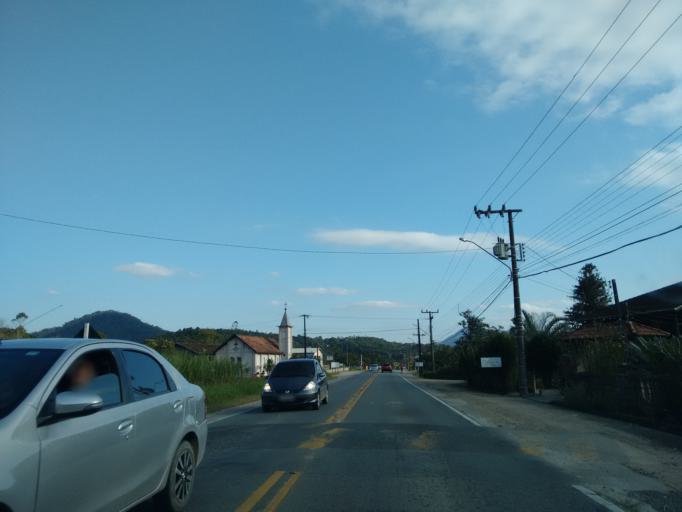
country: BR
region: Santa Catarina
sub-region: Pomerode
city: Pomerode
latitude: -26.6812
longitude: -49.1472
